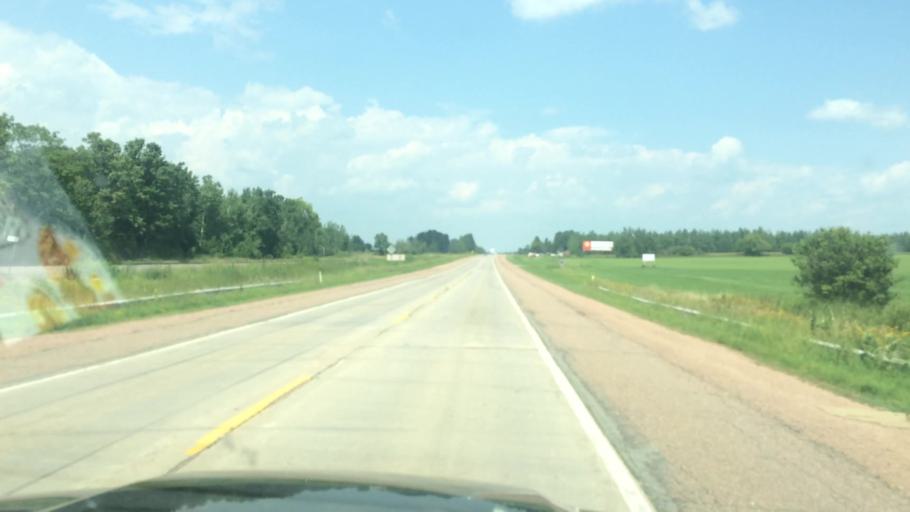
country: US
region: Wisconsin
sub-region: Clark County
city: Colby
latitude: 44.8744
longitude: -90.3157
